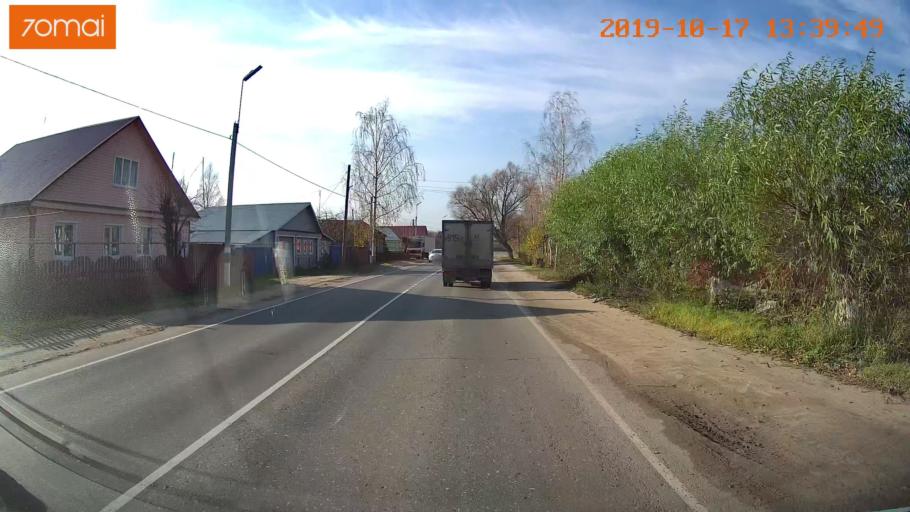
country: RU
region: Rjazan
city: Tuma
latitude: 55.1464
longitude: 40.5808
